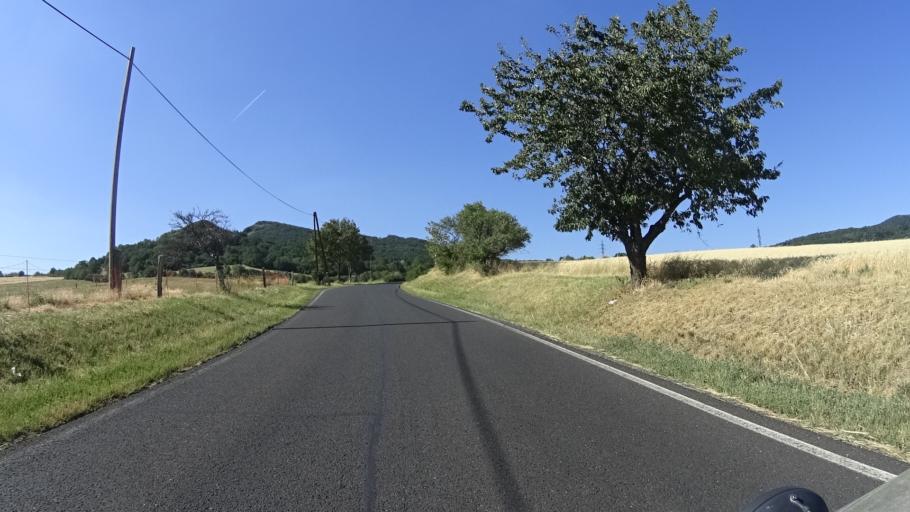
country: CZ
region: Ustecky
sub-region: Okres Litomerice
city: Litomerice
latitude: 50.5595
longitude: 14.1221
